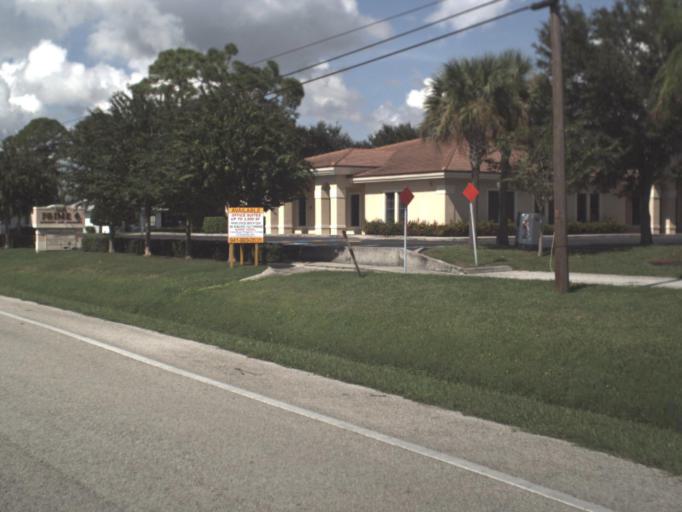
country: US
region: Florida
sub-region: Sarasota County
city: Laurel
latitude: 27.1597
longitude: -82.4719
